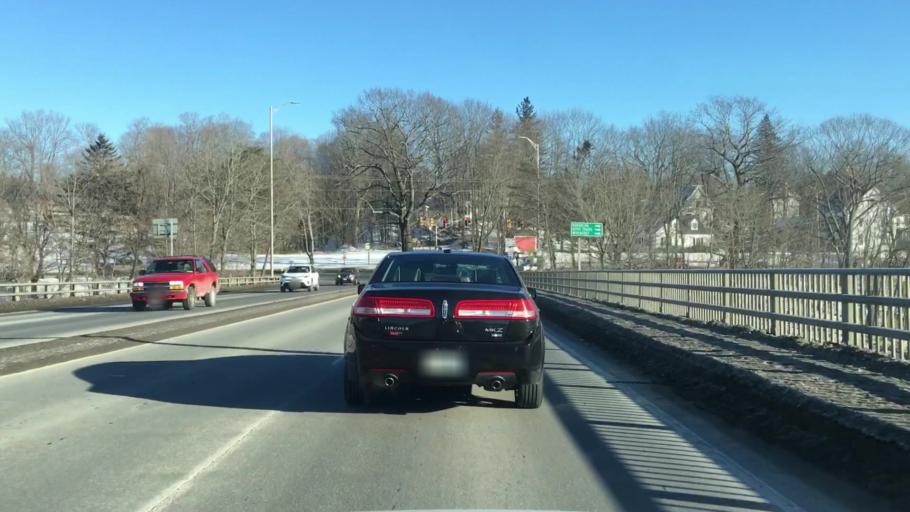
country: US
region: Maine
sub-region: Kennebec County
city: Randolph
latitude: 44.2332
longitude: -69.7692
